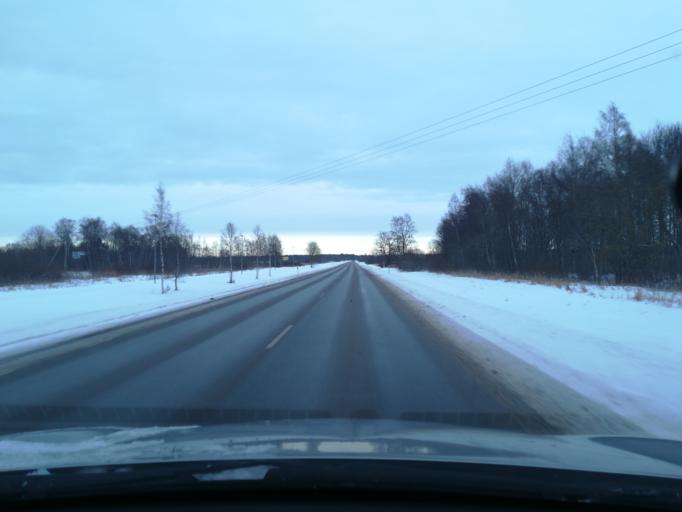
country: EE
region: Harju
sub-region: Harku vald
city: Tabasalu
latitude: 59.4490
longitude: 24.3906
